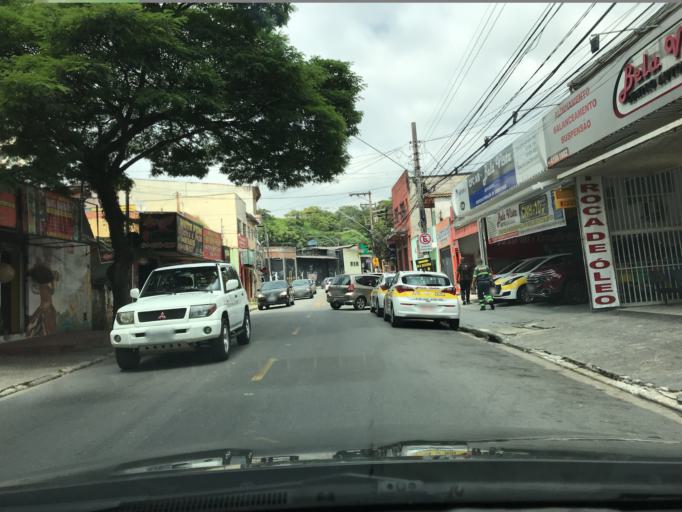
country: BR
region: Sao Paulo
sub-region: Barueri
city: Barueri
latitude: -23.5033
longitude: -46.8686
